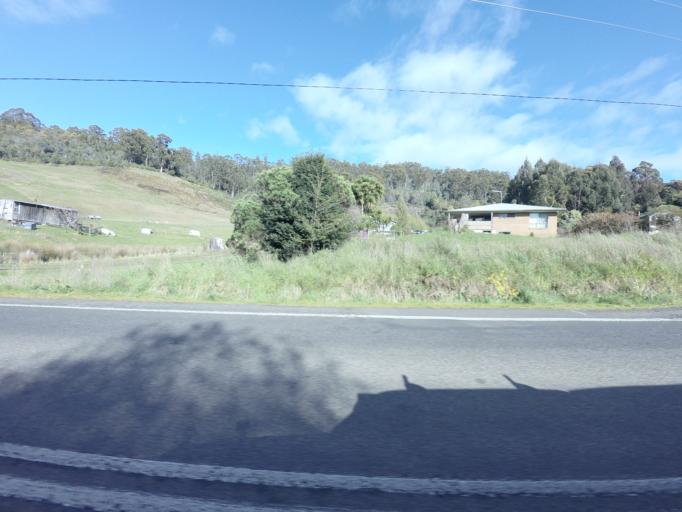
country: AU
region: Tasmania
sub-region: Huon Valley
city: Geeveston
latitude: -43.3036
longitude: 147.0073
